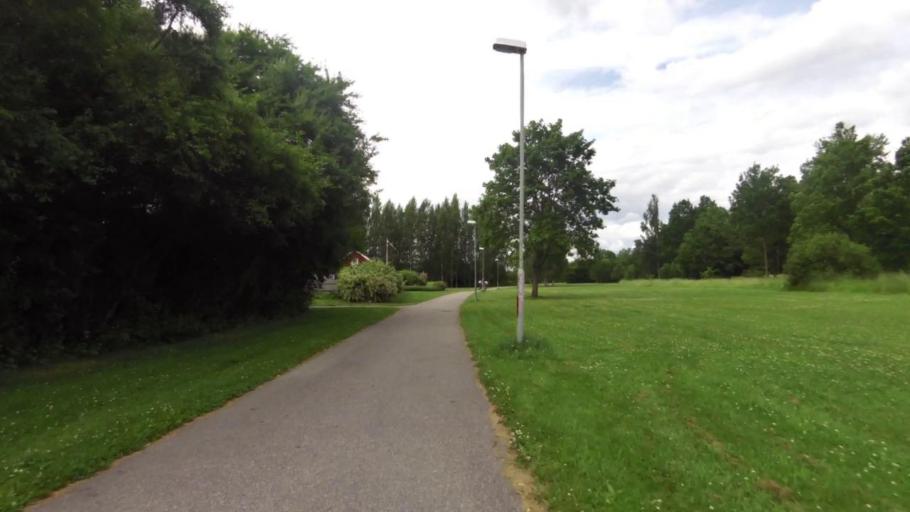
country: SE
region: OEstergoetland
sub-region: Linkopings Kommun
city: Malmslatt
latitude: 58.4163
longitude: 15.5667
